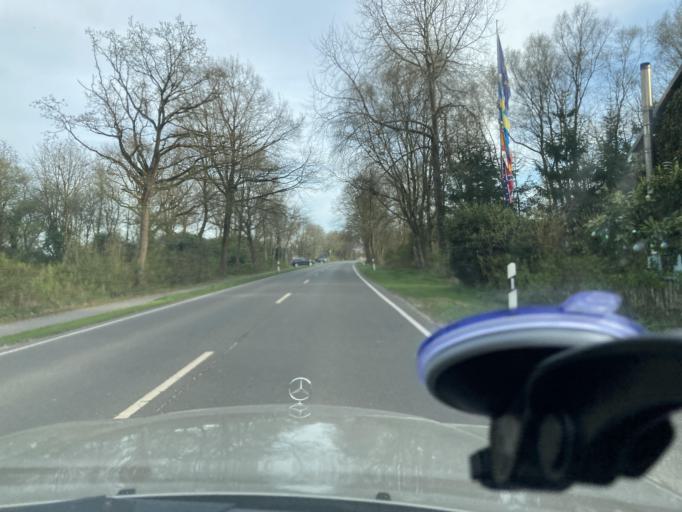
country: DE
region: Schleswig-Holstein
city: Stelle-Wittenwurth
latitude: 54.2659
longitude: 9.0504
